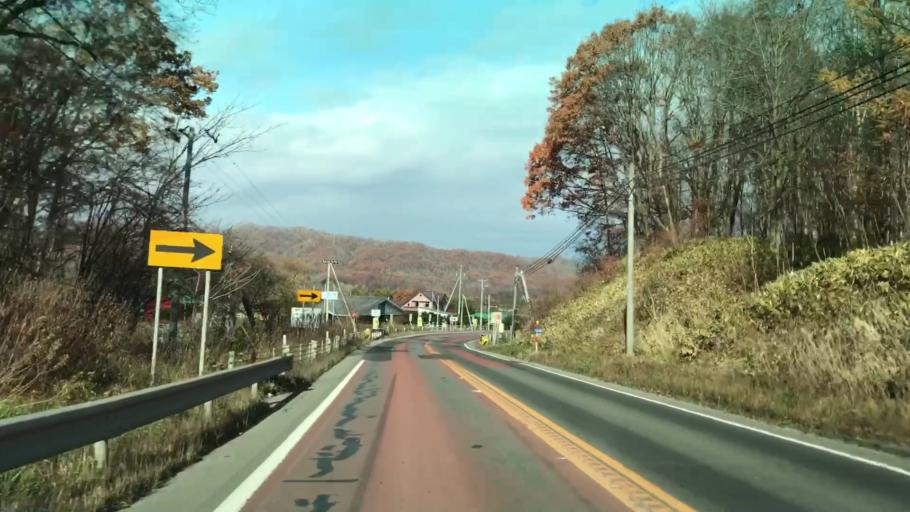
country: JP
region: Hokkaido
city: Shizunai-furukawacho
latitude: 42.6100
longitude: 142.1478
